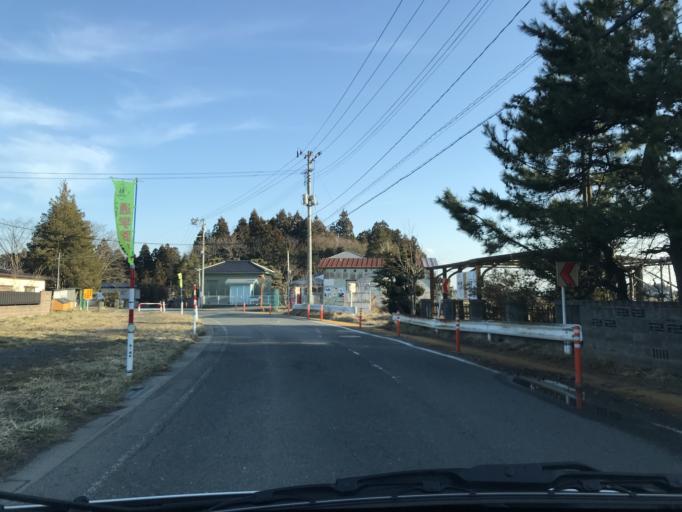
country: JP
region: Iwate
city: Kitakami
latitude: 39.2149
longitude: 141.1117
